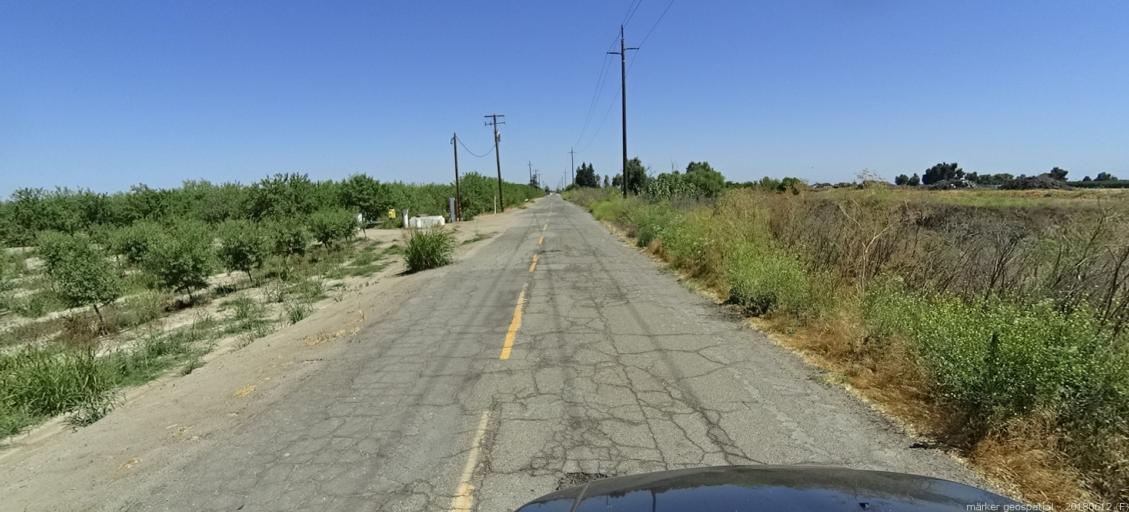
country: US
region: California
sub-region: Madera County
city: Chowchilla
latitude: 37.0142
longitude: -120.3286
